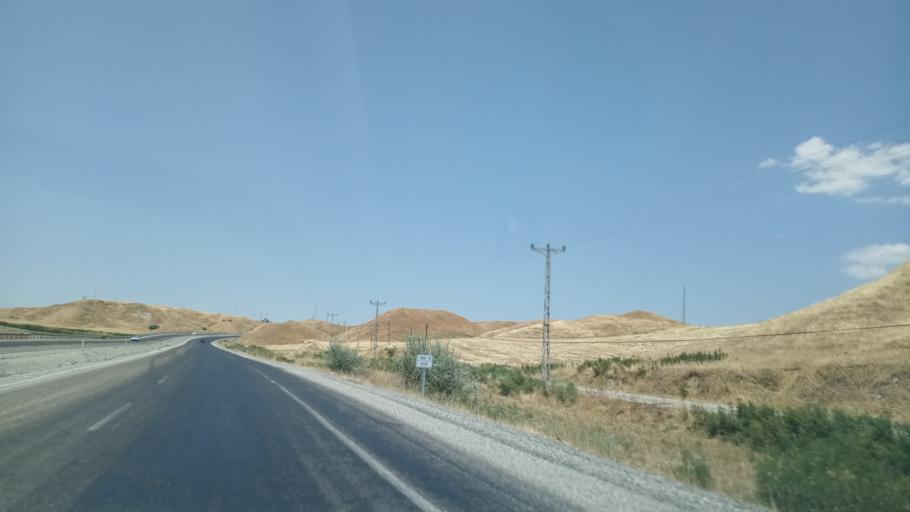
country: TR
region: Batman
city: Bekirhan
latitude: 38.1540
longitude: 41.3818
